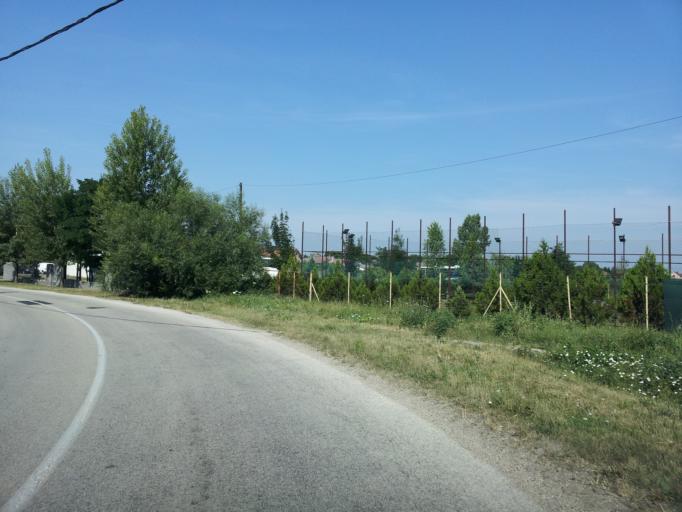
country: HU
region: Fejer
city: Lovasbereny
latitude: 47.3167
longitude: 18.5517
